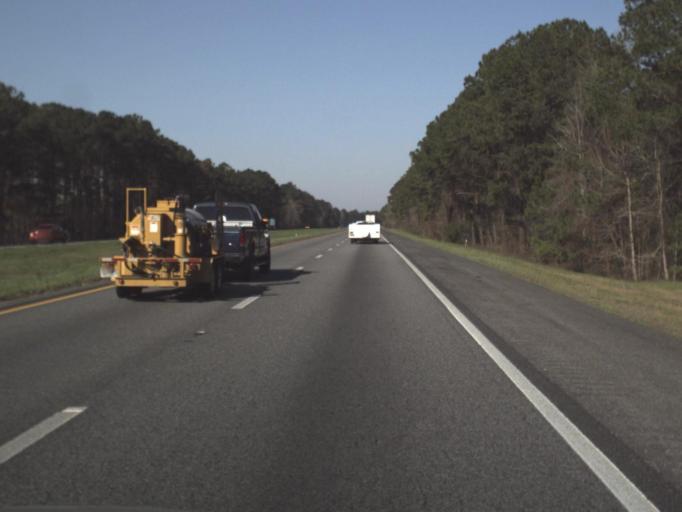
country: US
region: Florida
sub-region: Jefferson County
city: Monticello
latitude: 30.4786
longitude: -83.9231
